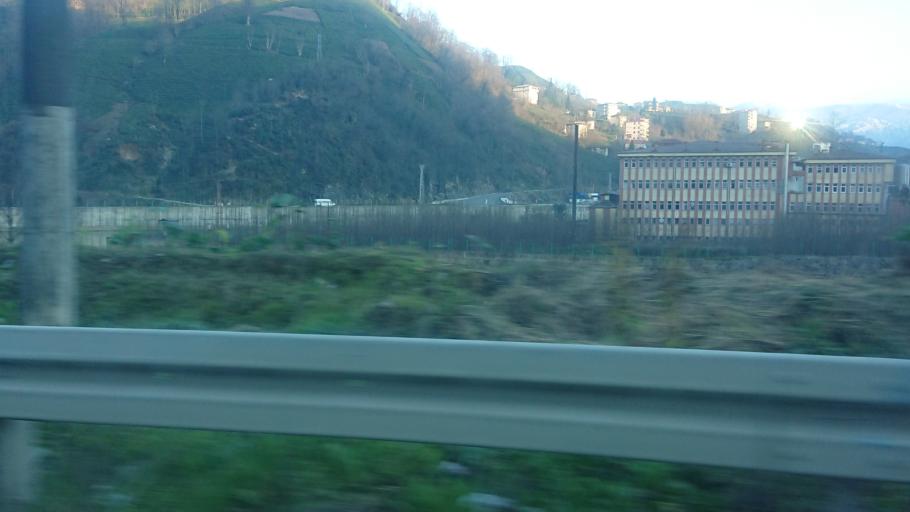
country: TR
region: Rize
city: Gundogdu
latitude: 41.0205
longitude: 40.5747
